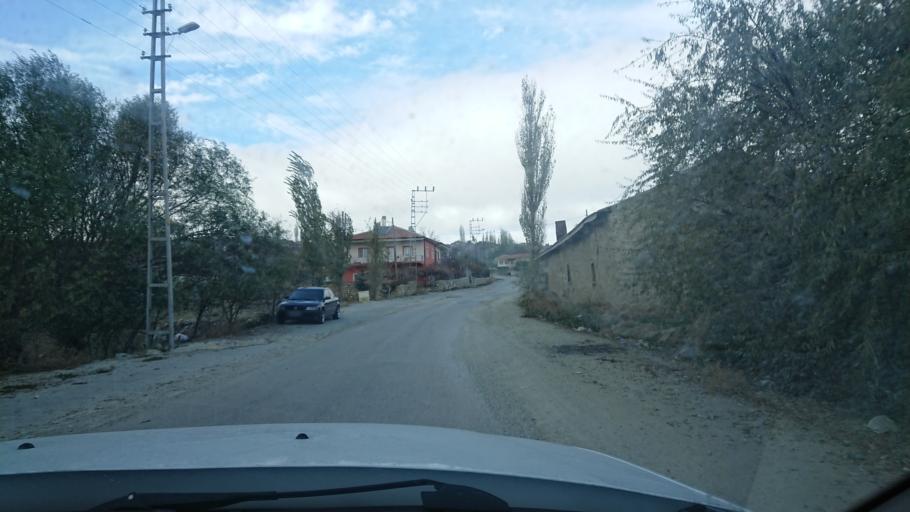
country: TR
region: Aksaray
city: Ortakoy
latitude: 38.7569
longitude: 34.0123
